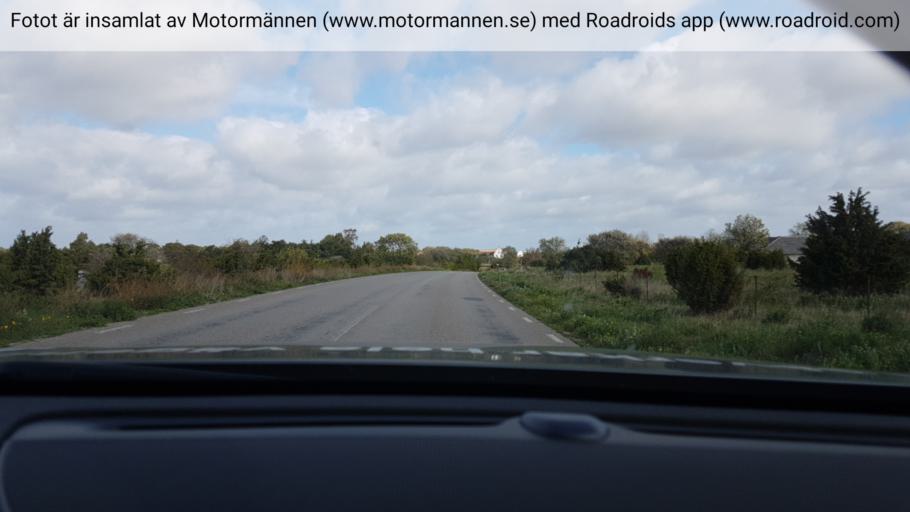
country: SE
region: Gotland
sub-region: Gotland
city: Slite
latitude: 57.9248
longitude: 19.1434
